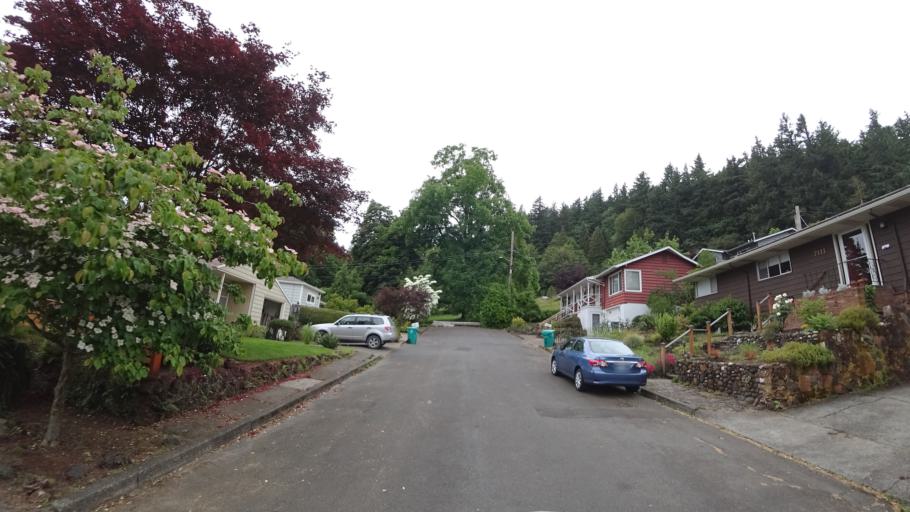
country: US
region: Oregon
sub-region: Multnomah County
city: Lents
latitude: 45.5083
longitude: -122.5897
